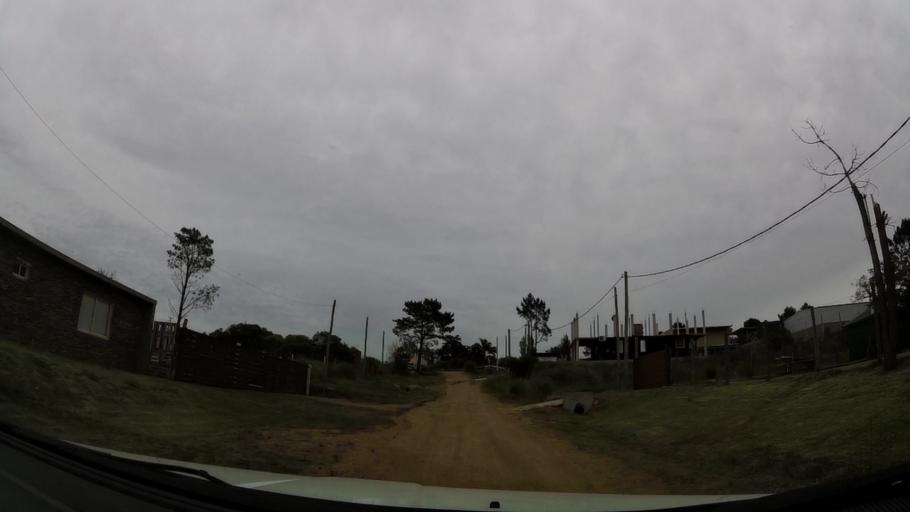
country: UY
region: Maldonado
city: Maldonado
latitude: -34.8919
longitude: -54.9898
